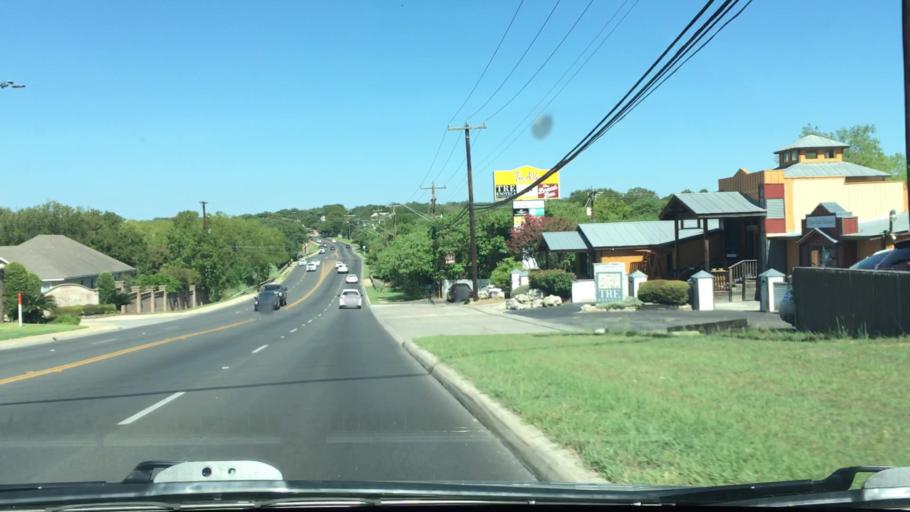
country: US
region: Texas
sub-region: Bexar County
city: Hollywood Park
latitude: 29.5785
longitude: -98.4998
